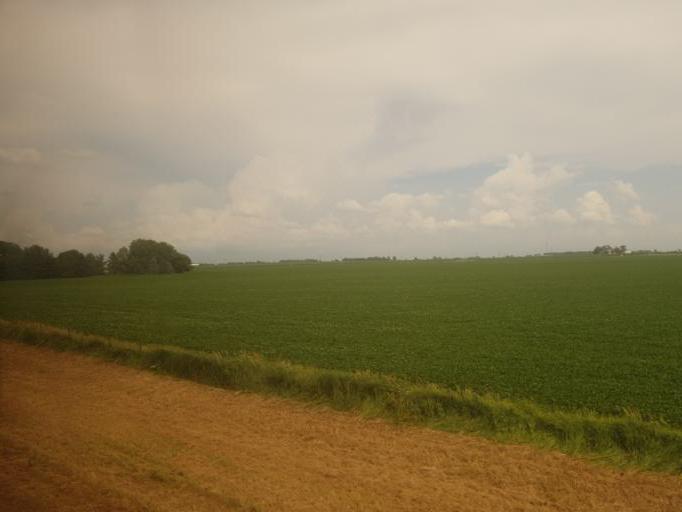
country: US
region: Illinois
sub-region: Knox County
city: Galesburg
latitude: 40.9175
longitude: -90.4124
